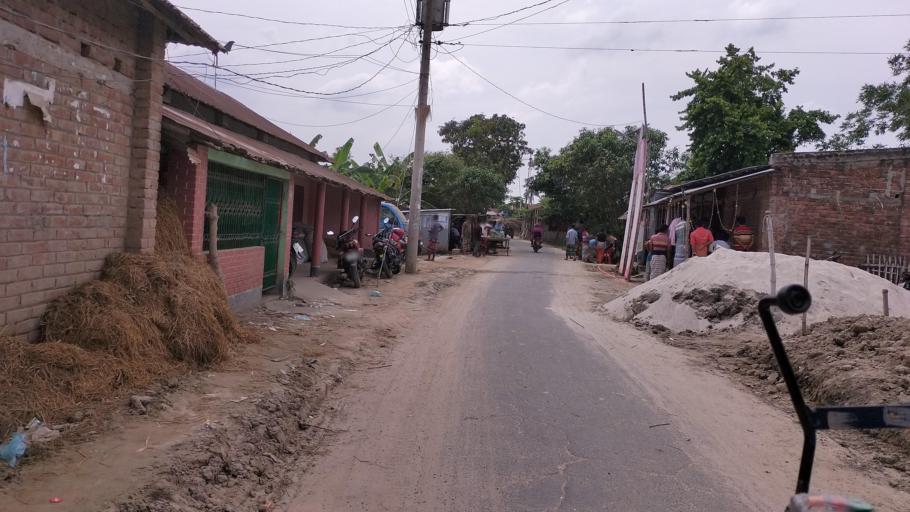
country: BD
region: Rajshahi
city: Rajshahi
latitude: 24.5255
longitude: 88.6153
